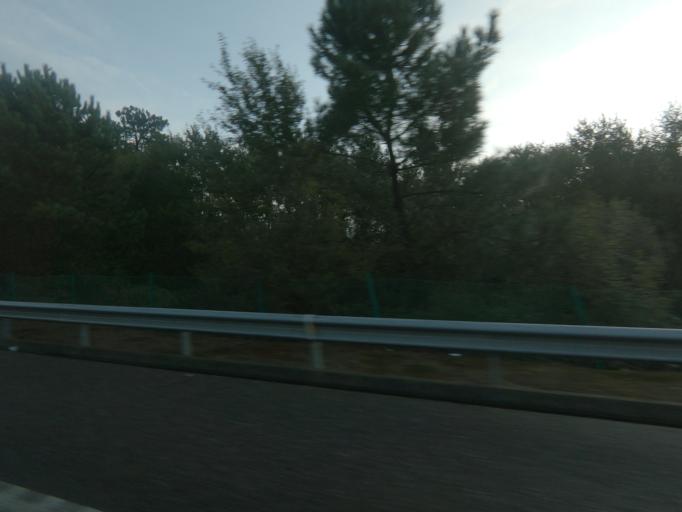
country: ES
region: Galicia
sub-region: Provincia de Pontevedra
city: Tui
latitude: 42.0968
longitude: -8.6438
